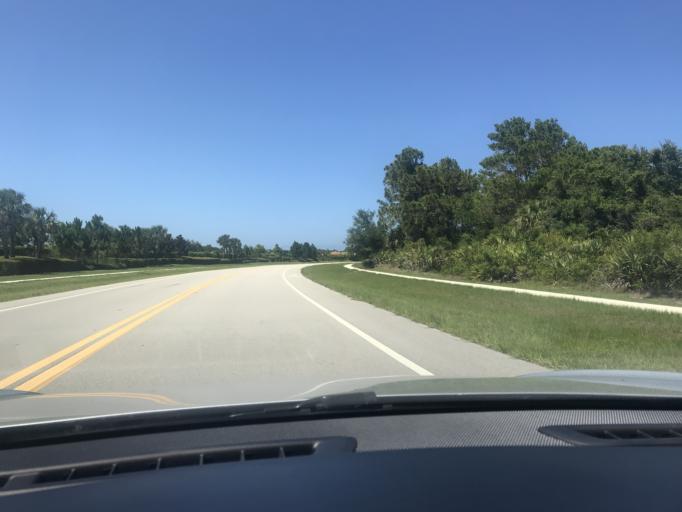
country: US
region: Florida
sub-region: Indian River County
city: Gifford
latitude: 27.6849
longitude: -80.4294
